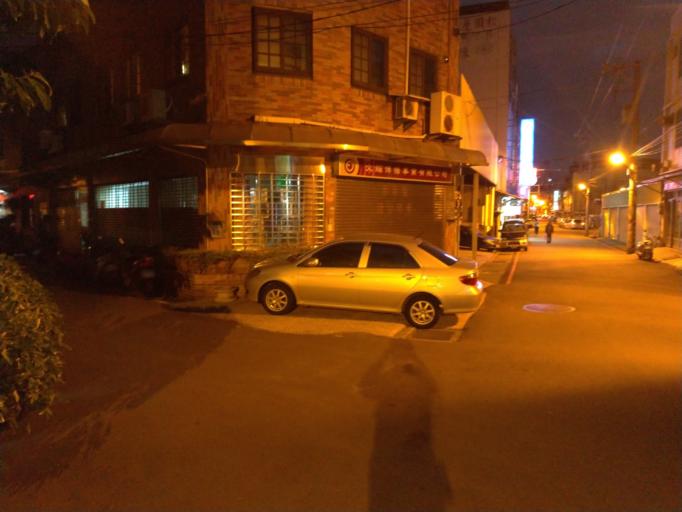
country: TW
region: Taiwan
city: Taoyuan City
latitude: 24.9753
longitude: 121.2561
